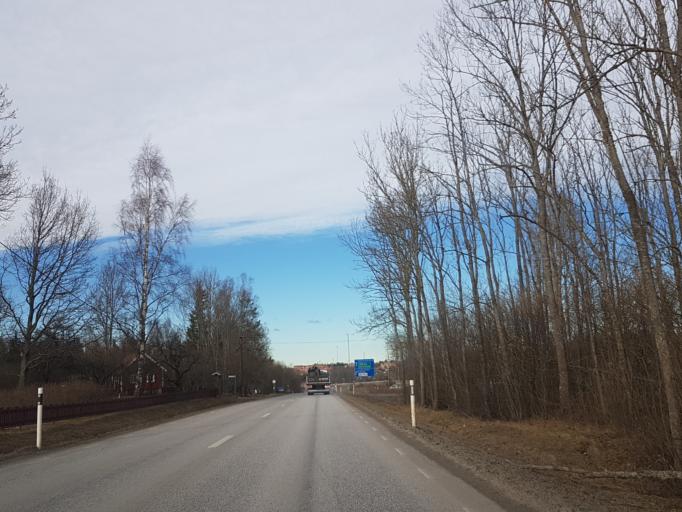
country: SE
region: Stockholm
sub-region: Norrtalje Kommun
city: Norrtalje
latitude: 59.7366
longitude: 18.6860
